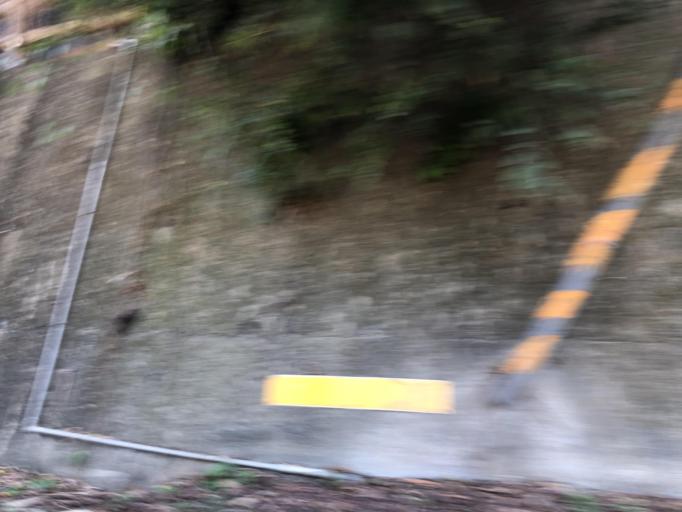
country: TW
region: Taiwan
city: Yujing
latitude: 23.0161
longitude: 120.3839
